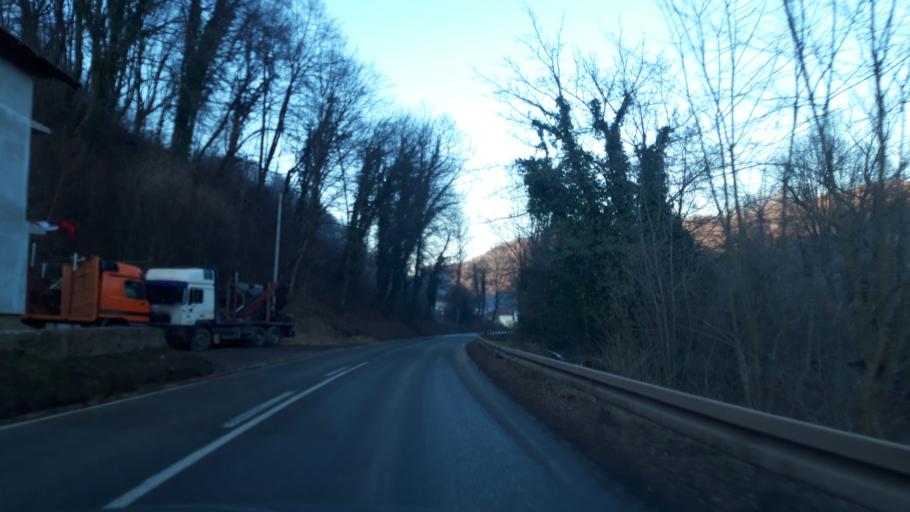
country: BA
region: Republika Srpska
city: Milici
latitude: 44.1792
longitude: 19.0739
